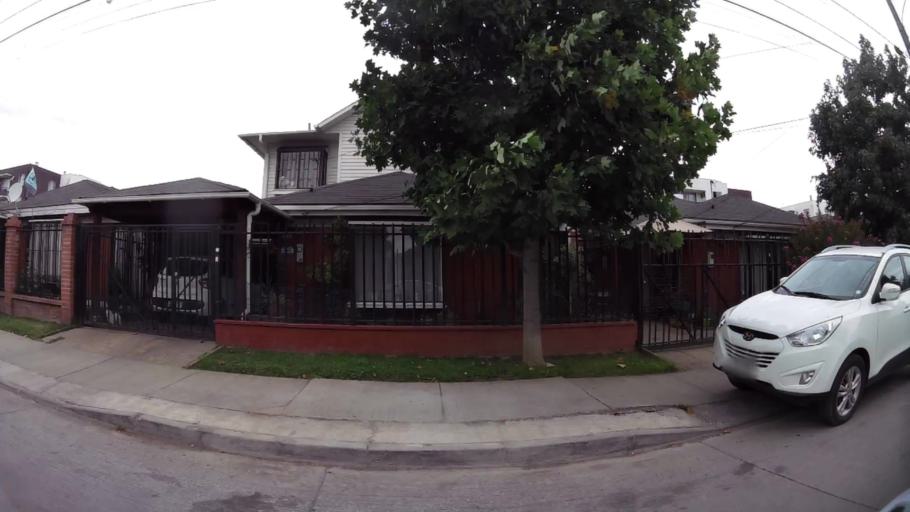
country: CL
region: O'Higgins
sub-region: Provincia de Cachapoal
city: Rancagua
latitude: -34.1423
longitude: -70.7394
